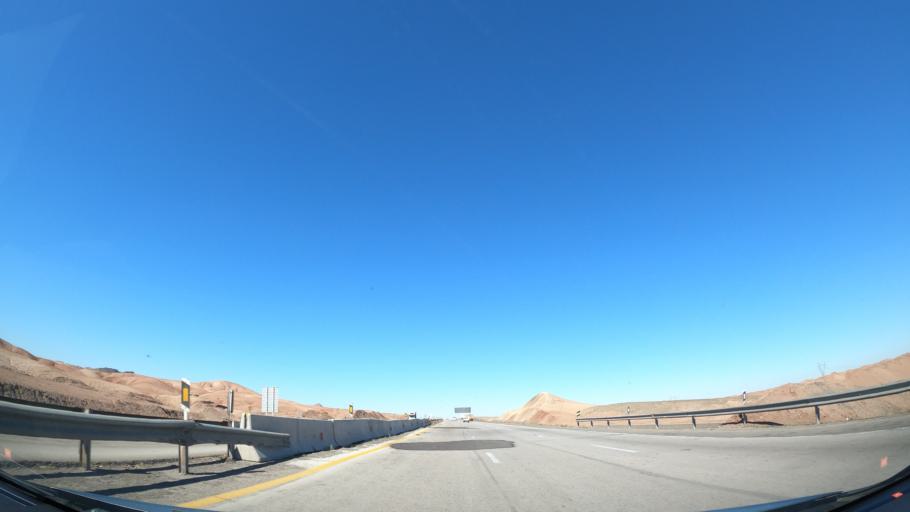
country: IR
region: Isfahan
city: Aran Bidgol
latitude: 34.3157
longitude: 51.2805
